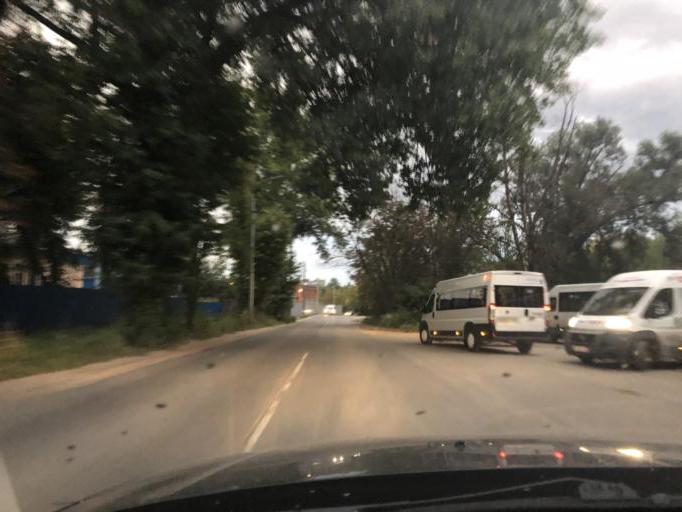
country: RU
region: Tula
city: Gorelki
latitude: 54.2262
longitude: 37.6073
